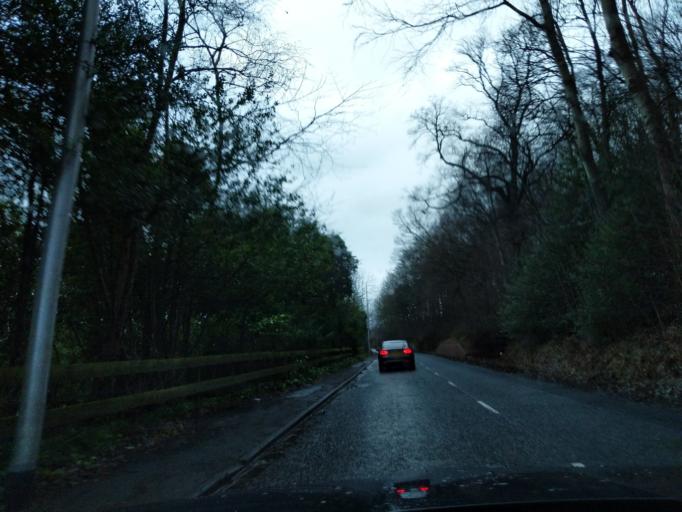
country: GB
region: Scotland
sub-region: The Scottish Borders
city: Galashiels
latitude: 55.6264
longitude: -2.8249
